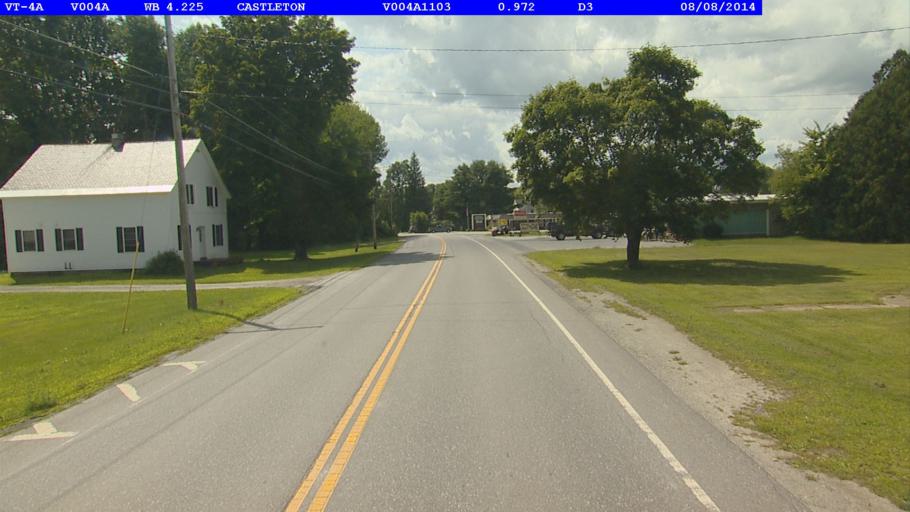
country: US
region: Vermont
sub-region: Rutland County
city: Fair Haven
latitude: 43.6074
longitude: -73.2248
